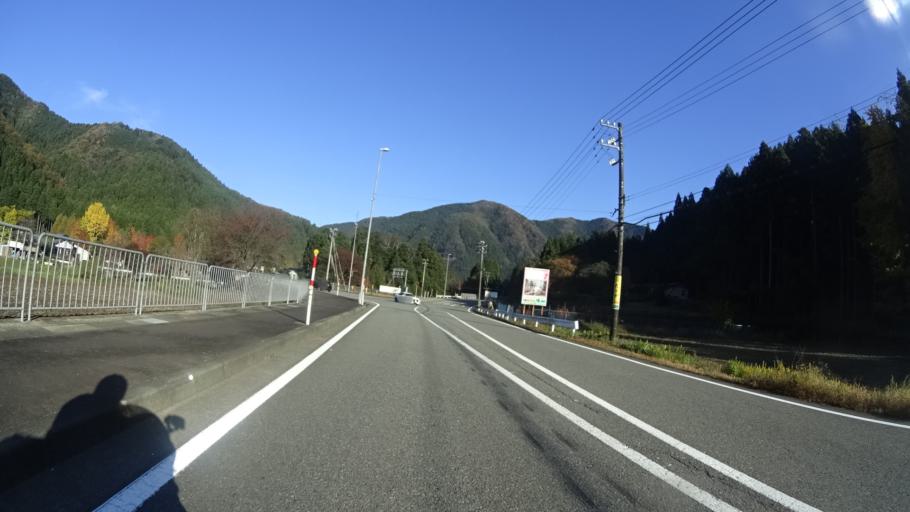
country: JP
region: Fukui
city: Maruoka
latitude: 36.1654
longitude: 136.3321
